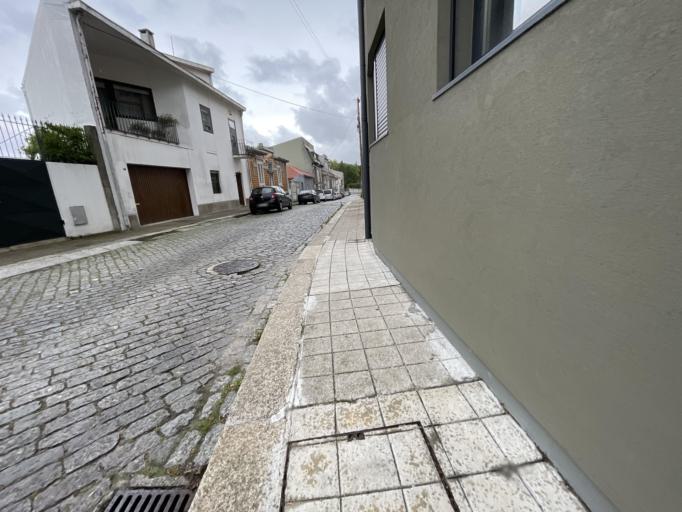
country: PT
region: Porto
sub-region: Porto
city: Porto
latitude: 41.1703
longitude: -8.6092
